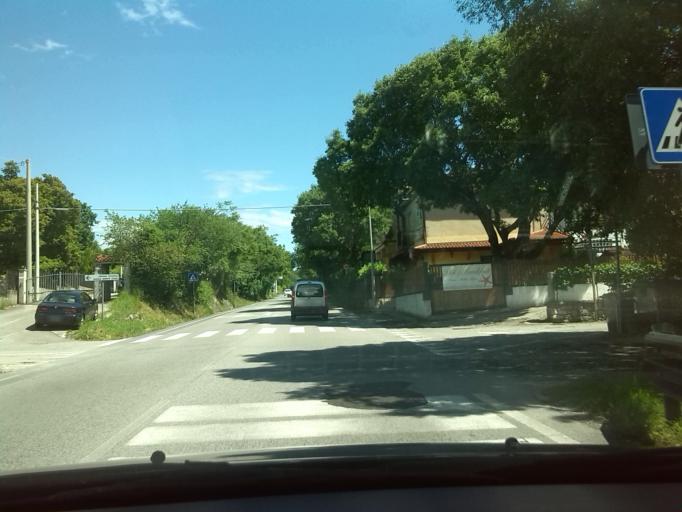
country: IT
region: Friuli Venezia Giulia
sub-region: Provincia di Trieste
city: Duino
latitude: 45.7761
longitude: 13.6038
